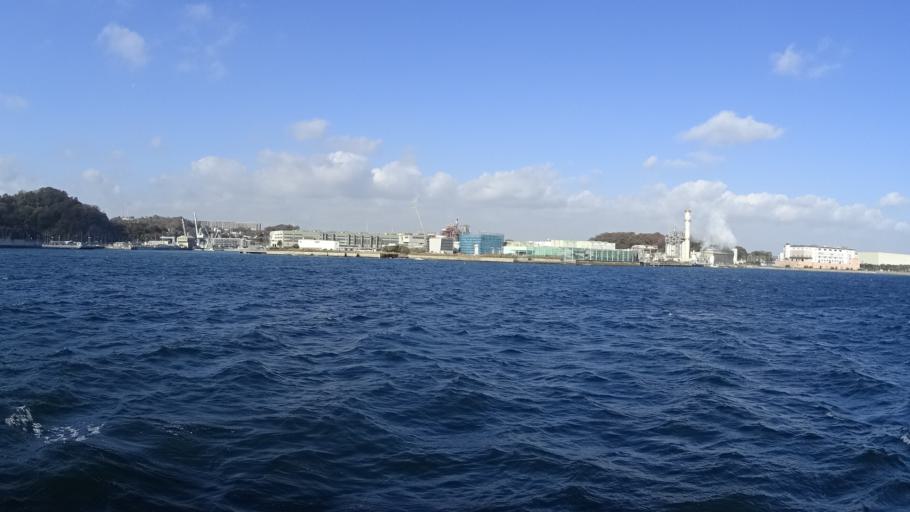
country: JP
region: Kanagawa
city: Yokosuka
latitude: 35.3061
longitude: 139.6471
